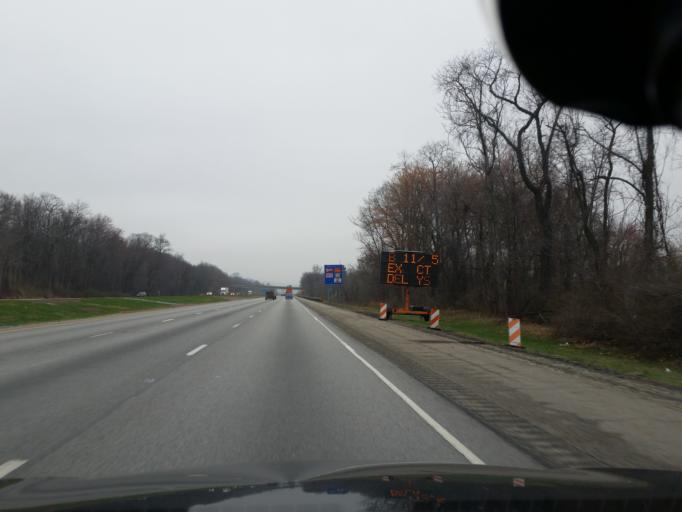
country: US
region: Pennsylvania
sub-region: Cumberland County
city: Enola
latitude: 40.3116
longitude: -76.9383
